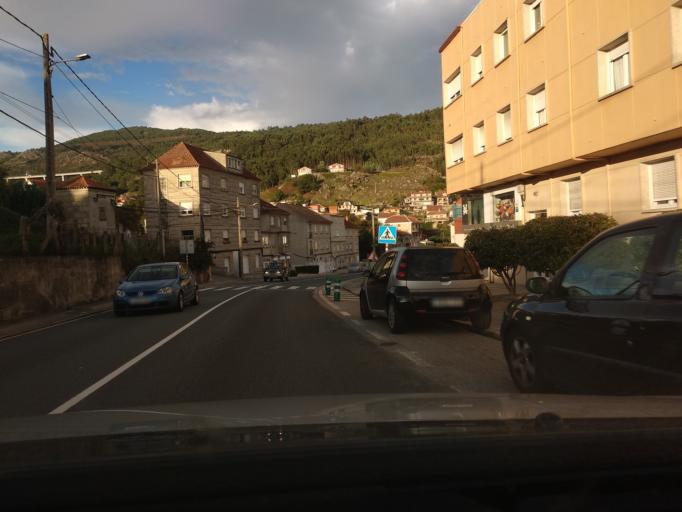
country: ES
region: Galicia
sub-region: Provincia de Pontevedra
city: Moana
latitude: 42.2890
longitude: -8.7198
